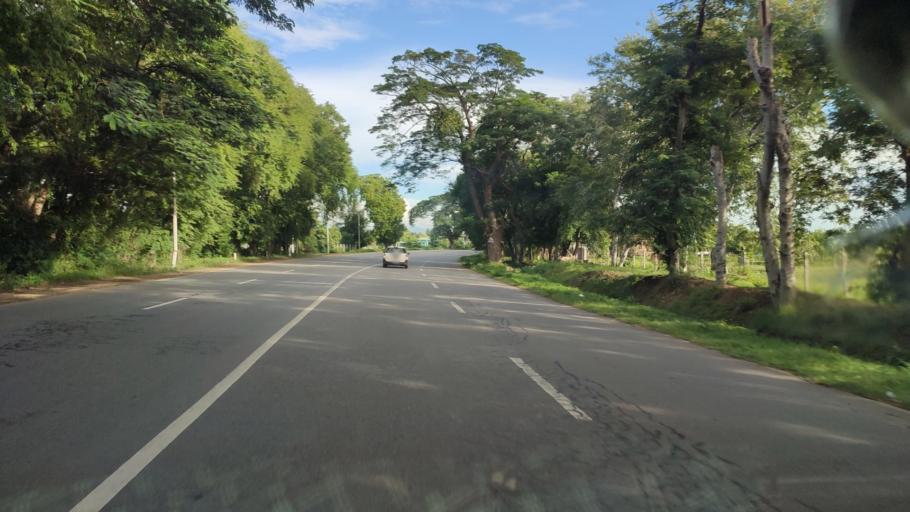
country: MM
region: Mandalay
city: Yamethin
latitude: 20.1848
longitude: 96.1873
